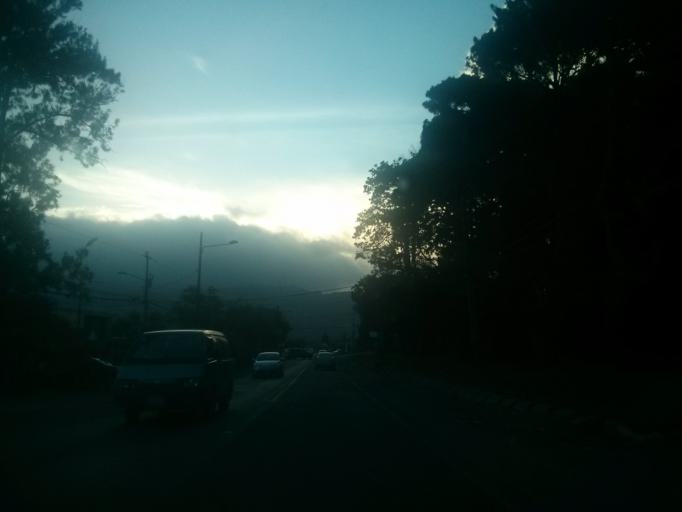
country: CR
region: Cartago
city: Cartago
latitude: 9.8793
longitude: -83.9312
